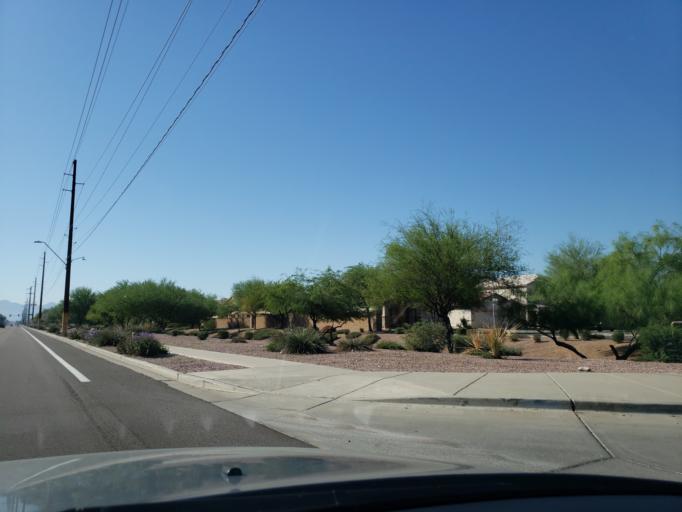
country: US
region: Arizona
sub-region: Maricopa County
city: Tolleson
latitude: 33.4754
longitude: -112.2553
